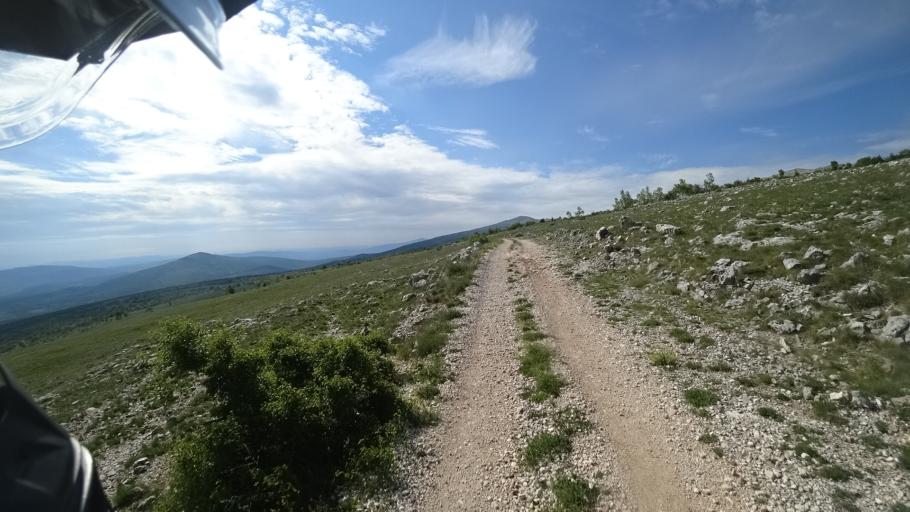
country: HR
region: Splitsko-Dalmatinska
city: Hrvace
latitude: 43.7737
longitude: 16.4581
